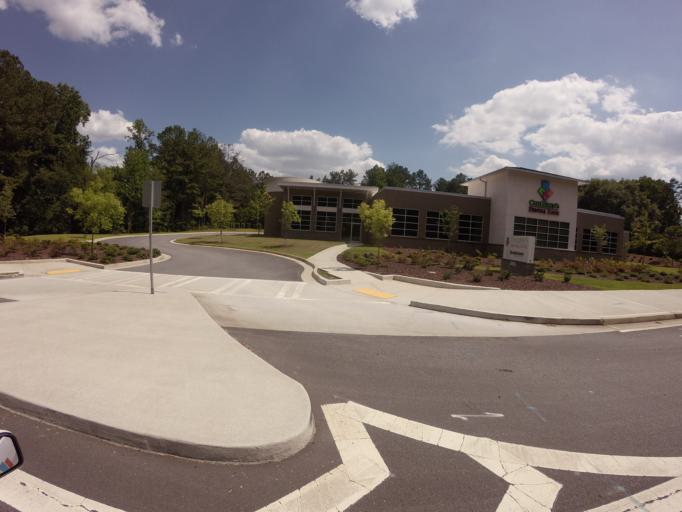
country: US
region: Georgia
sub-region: Fulton County
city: Johns Creek
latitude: 34.0239
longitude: -84.2590
